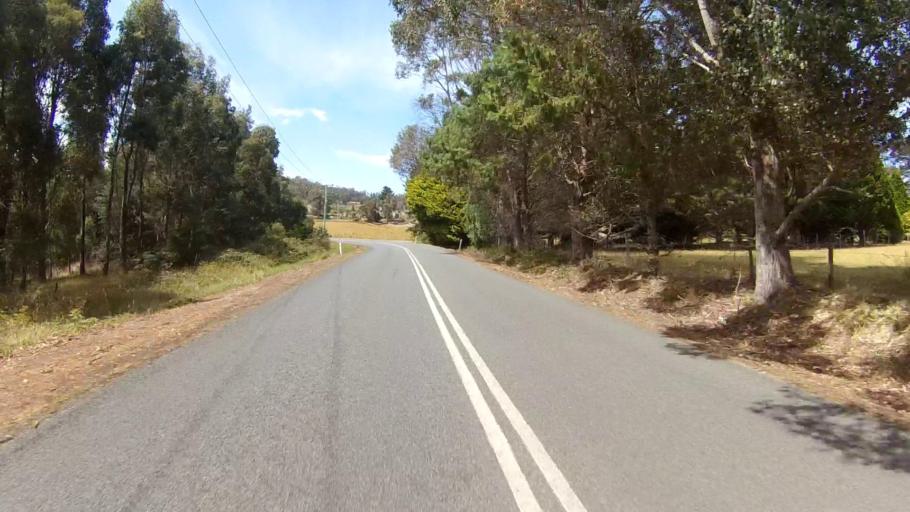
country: AU
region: Tasmania
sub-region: Huon Valley
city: Cygnet
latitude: -43.2153
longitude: 147.1205
